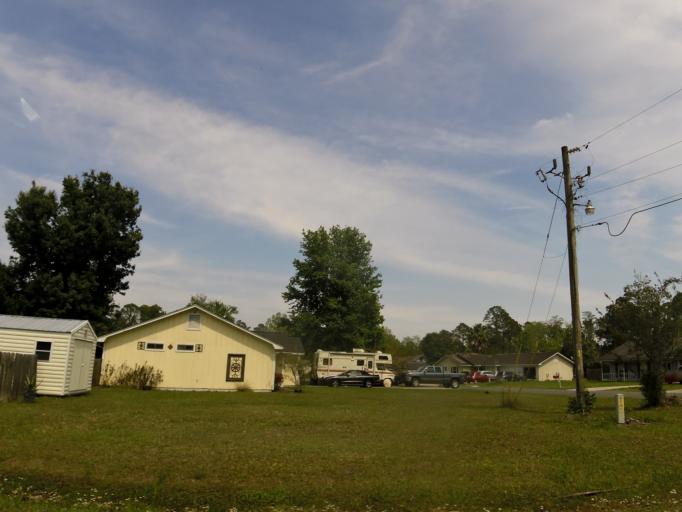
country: US
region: Georgia
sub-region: Camden County
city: Kingsland
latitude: 30.7664
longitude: -81.6602
